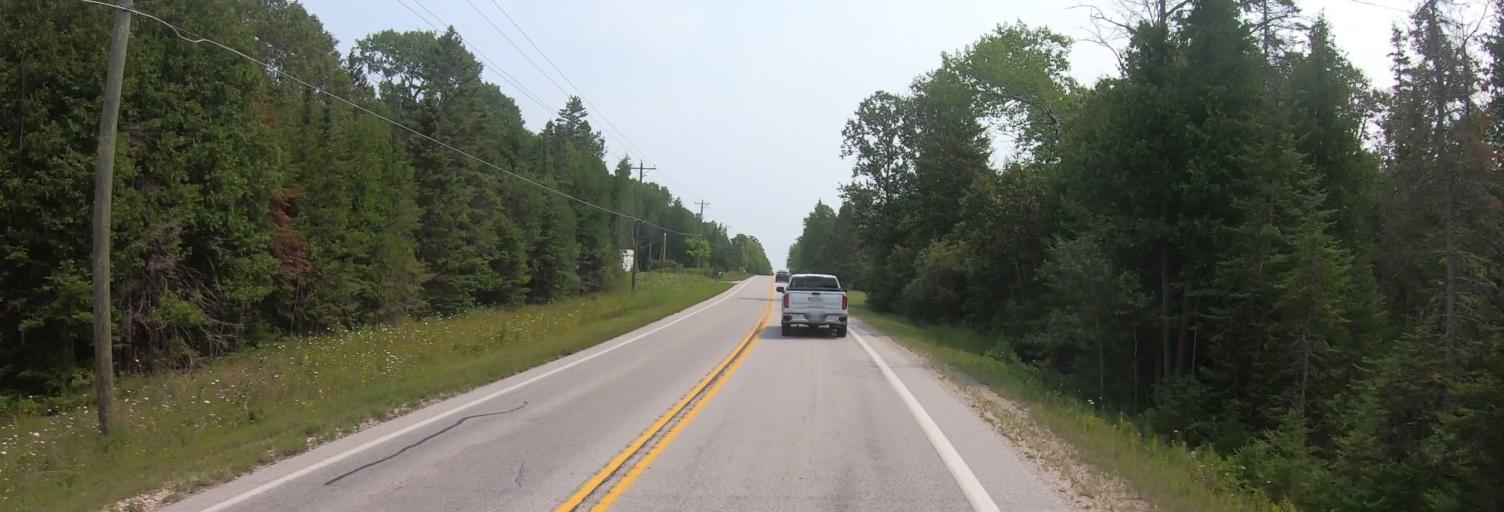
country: CA
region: Ontario
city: Thessalon
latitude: 45.9988
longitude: -83.7612
